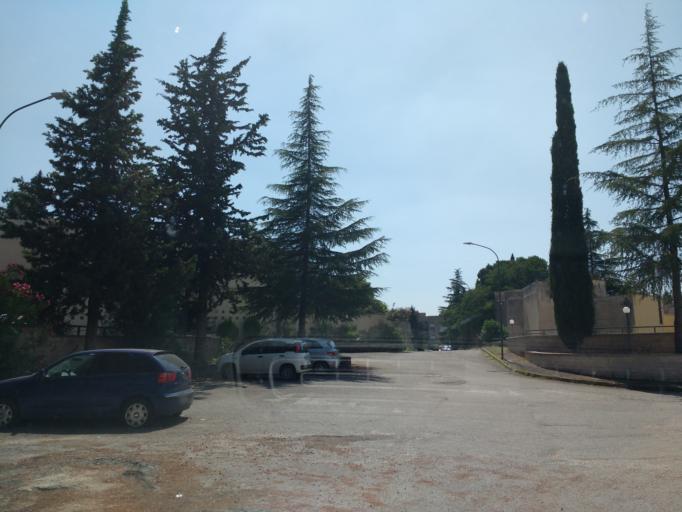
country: IT
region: Latium
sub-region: Citta metropolitana di Roma Capitale
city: Villa Adriana
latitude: 41.9513
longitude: 12.7820
